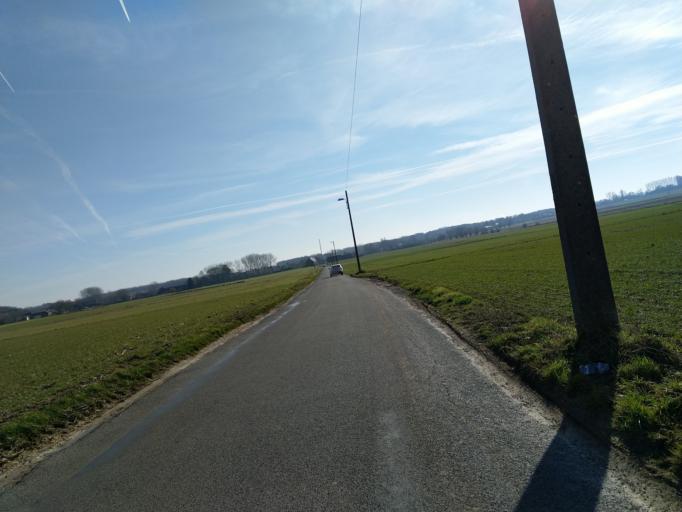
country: BE
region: Wallonia
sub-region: Province du Hainaut
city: Jurbise
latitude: 50.5259
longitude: 3.9539
